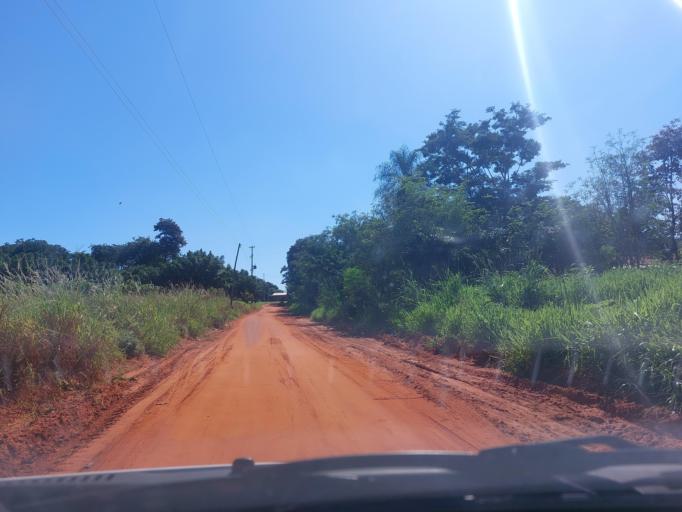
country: PY
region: San Pedro
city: Lima
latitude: -24.1638
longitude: -56.0134
